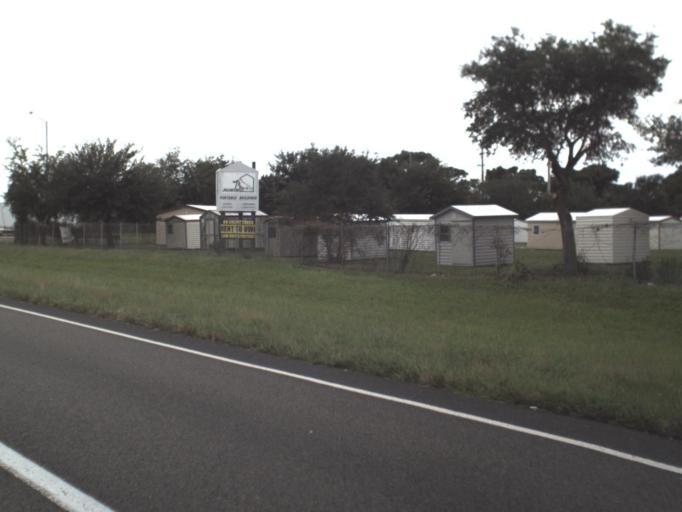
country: US
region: Florida
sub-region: Manatee County
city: Whitfield
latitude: 27.4192
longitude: -82.5330
